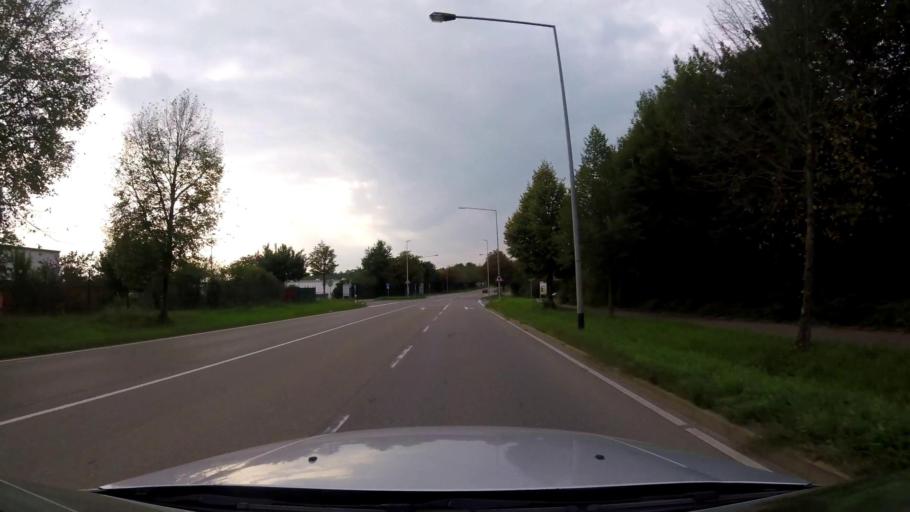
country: DE
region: Baden-Wuerttemberg
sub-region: Regierungsbezirk Stuttgart
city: Backnang
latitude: 48.9313
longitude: 9.4425
